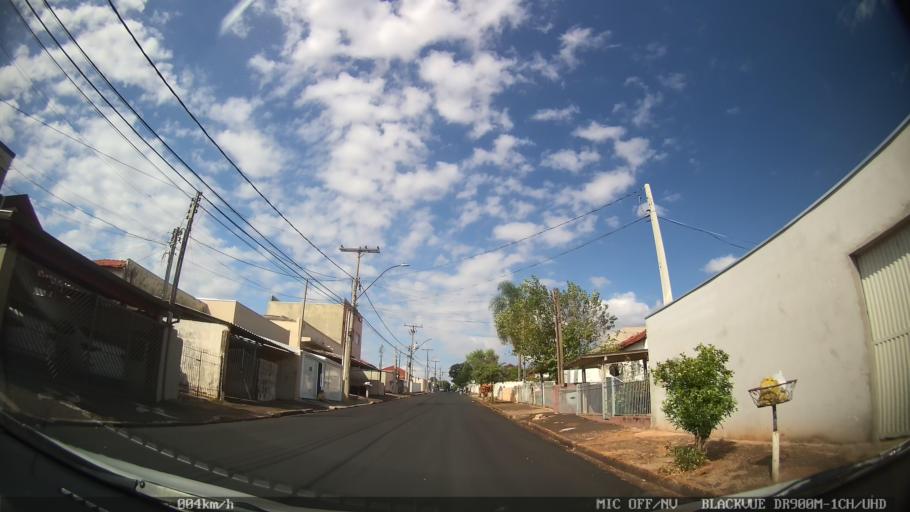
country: BR
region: Sao Paulo
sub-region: Americana
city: Americana
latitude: -22.7288
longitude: -47.3230
